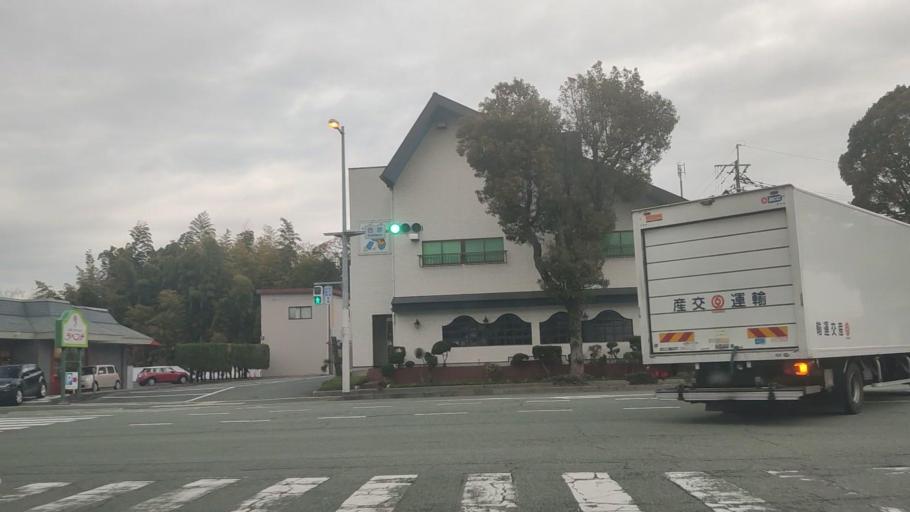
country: JP
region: Kumamoto
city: Kumamoto
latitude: 32.8167
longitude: 130.7523
